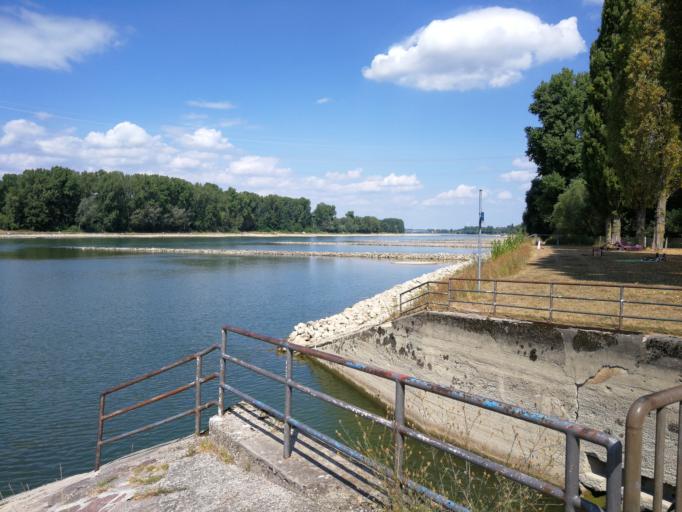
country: DE
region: Baden-Wuerttemberg
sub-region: Karlsruhe Region
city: Rheinstetten
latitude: 49.0016
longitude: 8.2923
